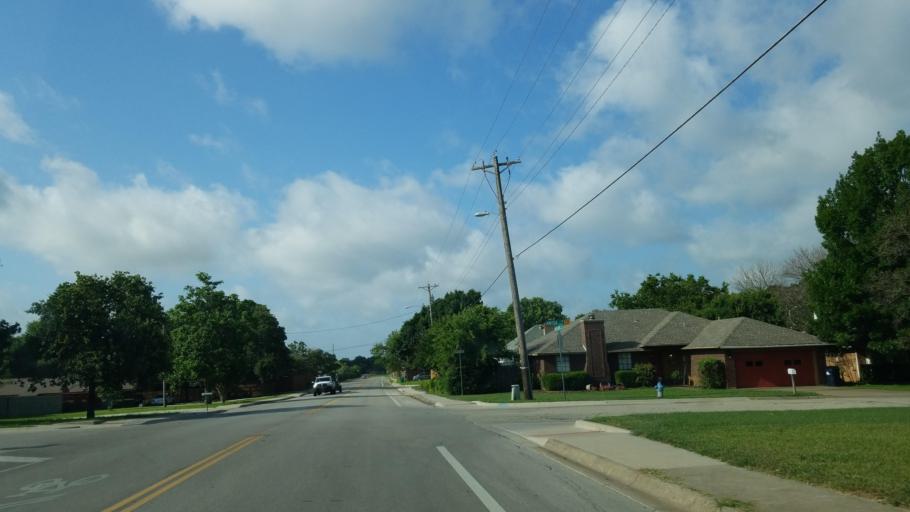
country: US
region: Texas
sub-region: Denton County
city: Denton
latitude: 33.2264
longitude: -97.0977
